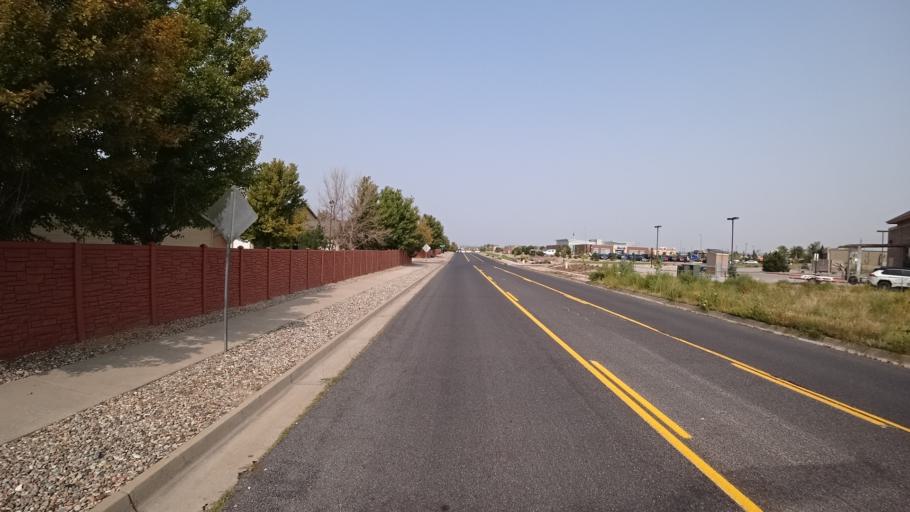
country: US
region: Colorado
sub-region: El Paso County
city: Cimarron Hills
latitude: 38.9231
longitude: -104.7207
